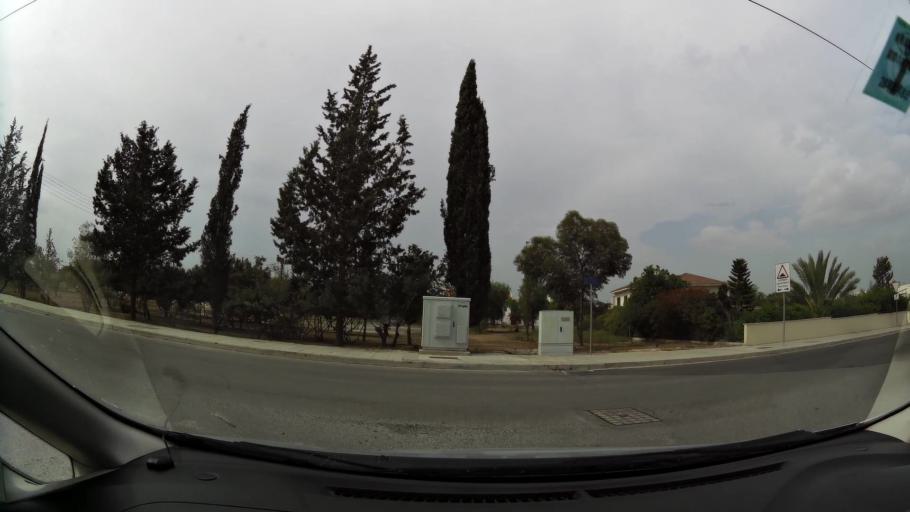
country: CY
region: Lefkosia
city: Geri
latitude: 35.0821
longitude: 33.3899
